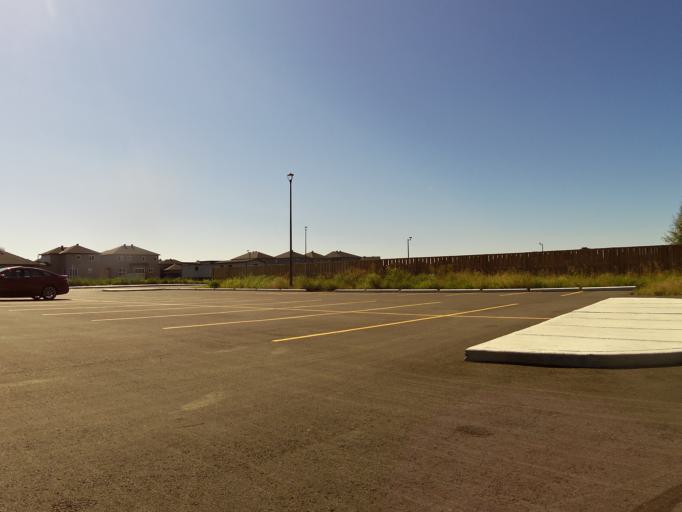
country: CA
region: Ontario
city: Casselman
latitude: 45.2679
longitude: -75.2847
